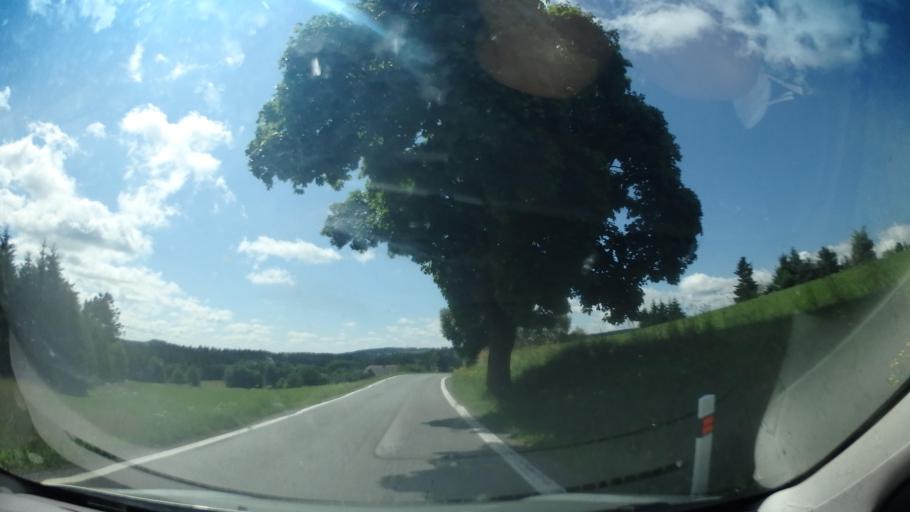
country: CZ
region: Vysocina
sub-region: Okres Zd'ar nad Sazavou
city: Nove Mesto na Morave
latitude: 49.6204
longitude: 16.0369
